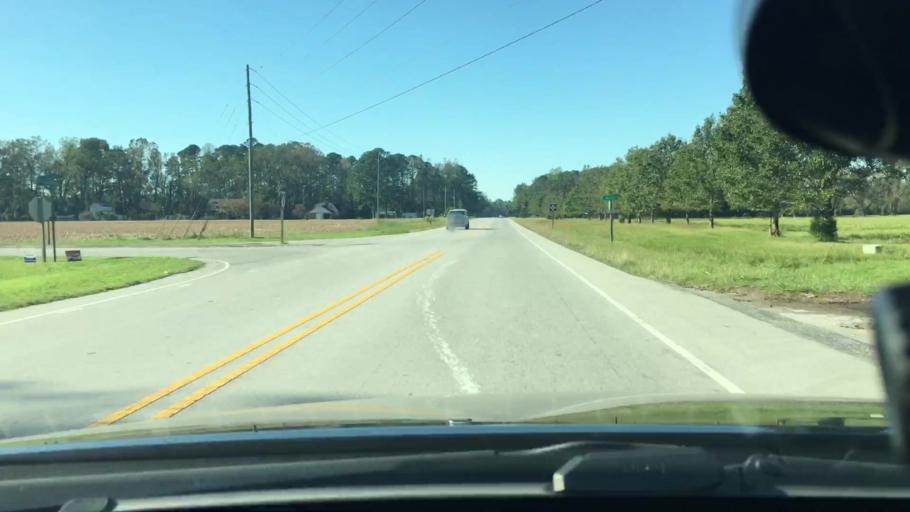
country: US
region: North Carolina
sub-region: Craven County
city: Trent Woods
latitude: 35.1655
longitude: -77.1212
